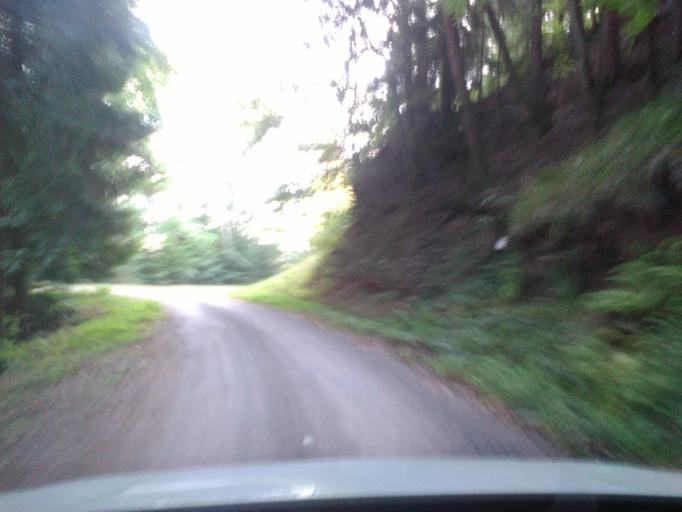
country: FR
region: Lorraine
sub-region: Departement des Vosges
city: Senones
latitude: 48.4059
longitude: 6.9763
